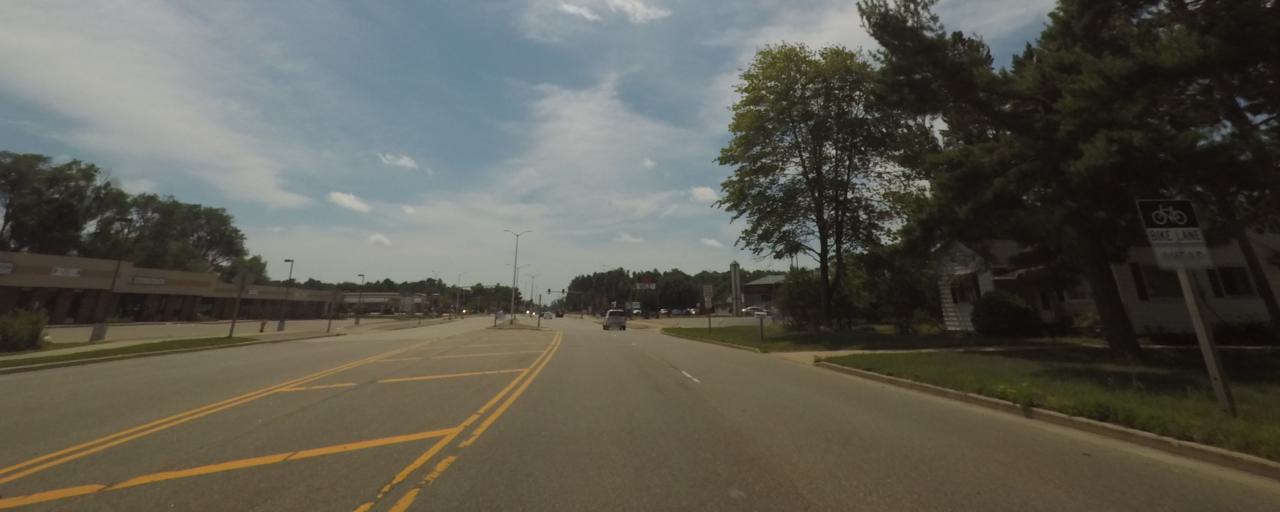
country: US
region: Wisconsin
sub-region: Portage County
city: Plover
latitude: 44.4709
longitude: -89.5473
